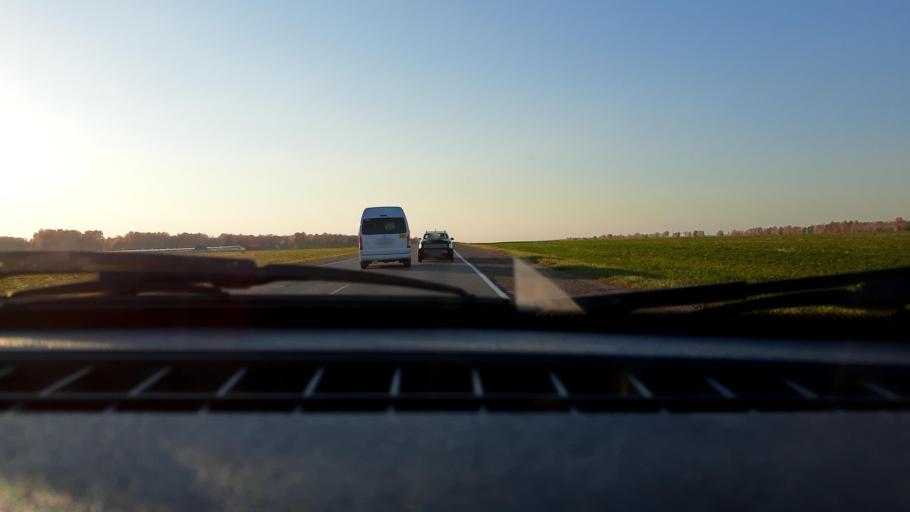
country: RU
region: Bashkortostan
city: Avdon
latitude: 54.8231
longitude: 55.6581
